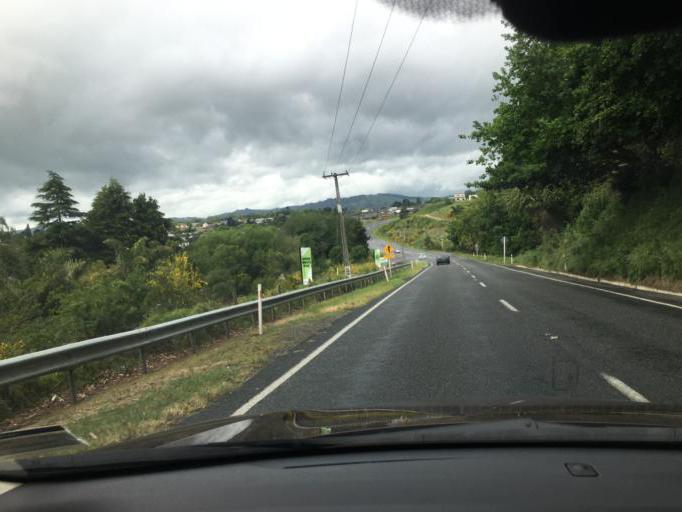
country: NZ
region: Waikato
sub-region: Waipa District
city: Cambridge
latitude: -37.9011
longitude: 175.4533
